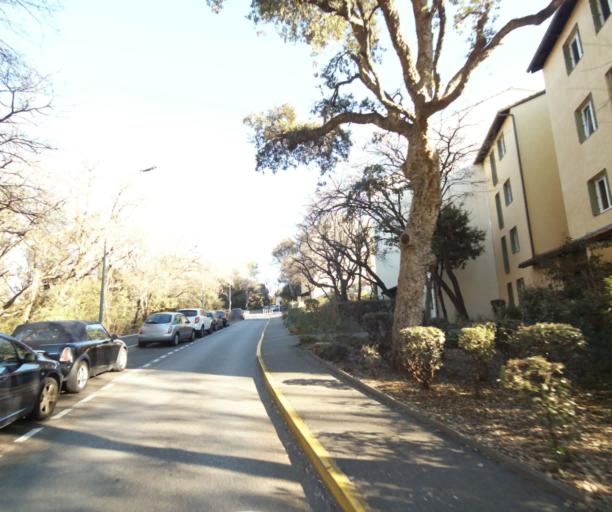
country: FR
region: Provence-Alpes-Cote d'Azur
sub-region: Departement des Alpes-Maritimes
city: Vallauris
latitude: 43.5962
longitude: 7.0659
